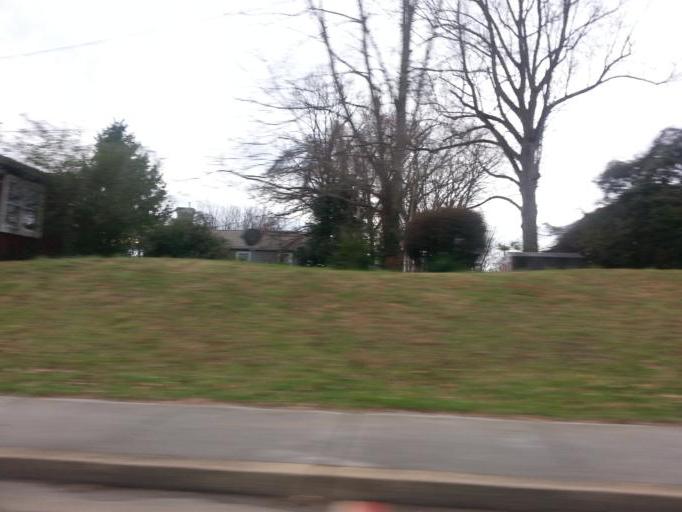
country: US
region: Tennessee
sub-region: Washington County
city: Johnson City
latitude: 36.3119
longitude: -82.3662
